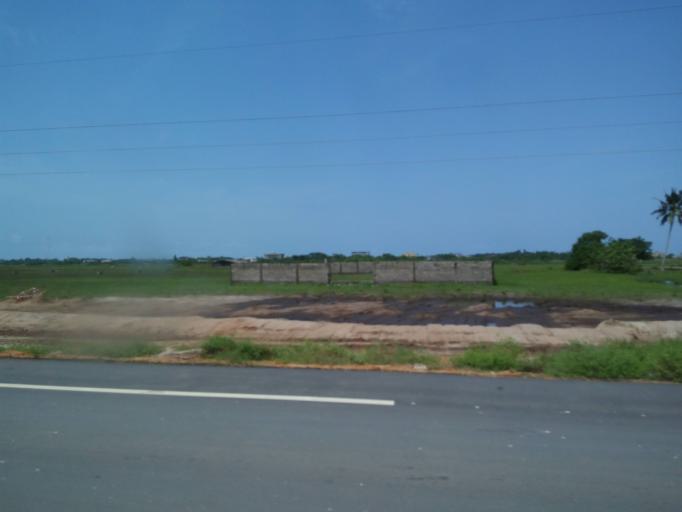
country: CI
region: Sud-Comoe
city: Grand-Bassam
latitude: 5.2295
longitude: -3.7512
